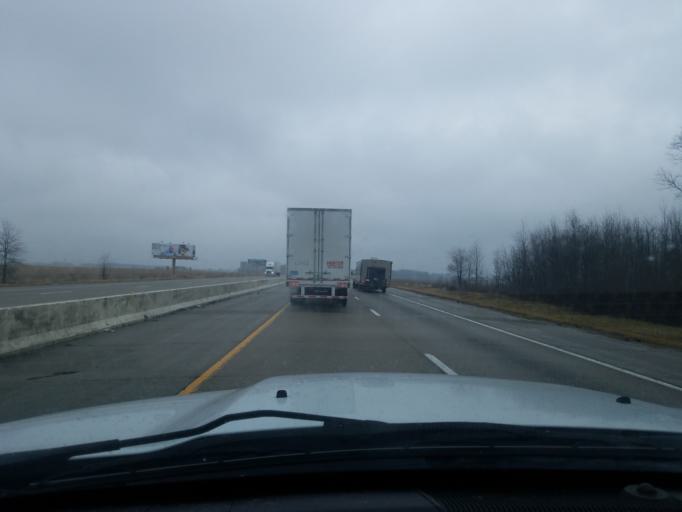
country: US
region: Indiana
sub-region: Wells County
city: Ossian
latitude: 40.9522
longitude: -85.2354
